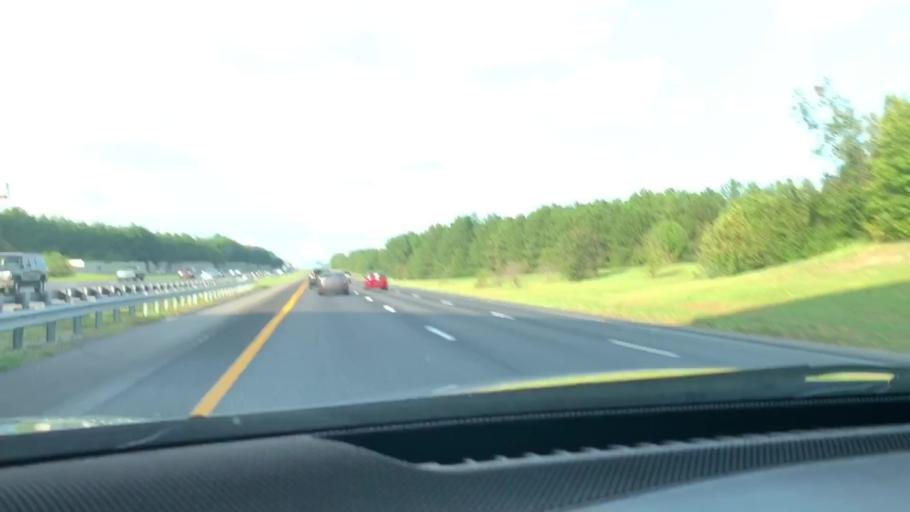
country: US
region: South Carolina
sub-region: Richland County
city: Woodfield
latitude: 34.0218
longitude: -80.9461
